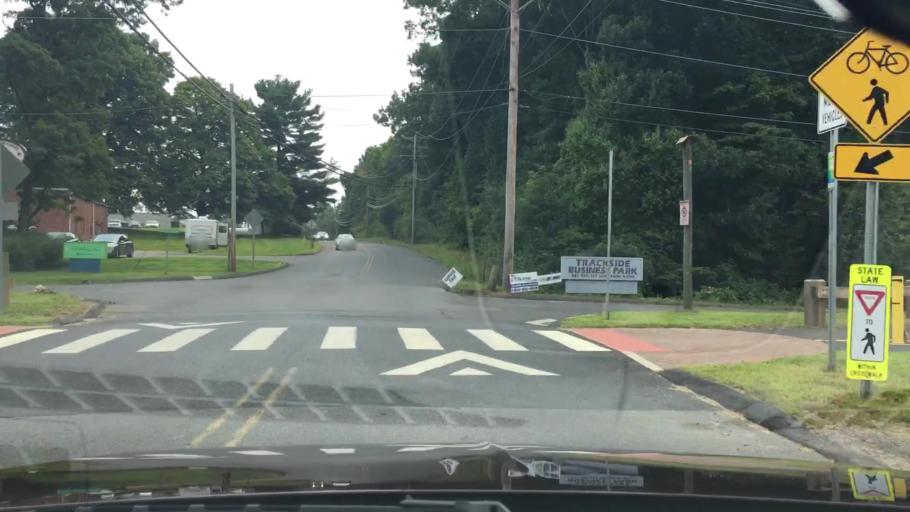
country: US
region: Connecticut
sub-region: New Haven County
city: Cheshire Village
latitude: 41.5358
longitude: -72.9027
